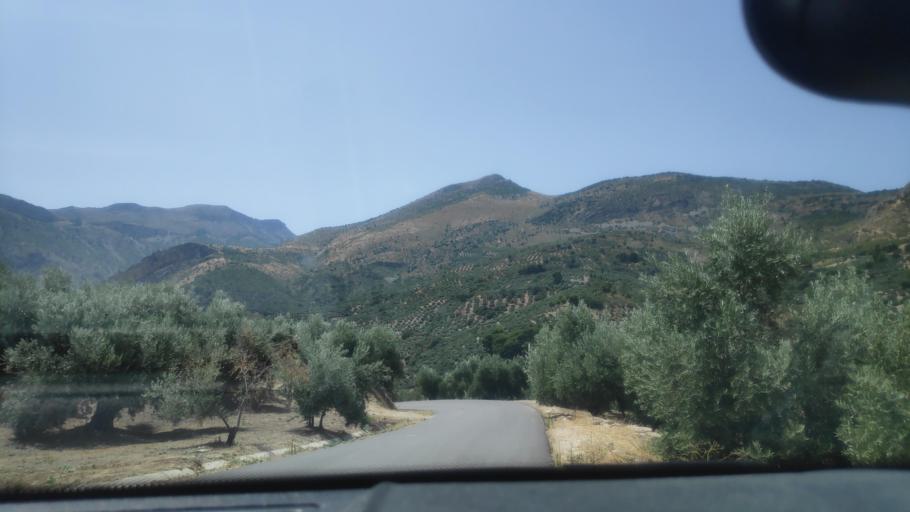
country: ES
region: Andalusia
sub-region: Provincia de Jaen
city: Torres
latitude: 37.7893
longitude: -3.4547
